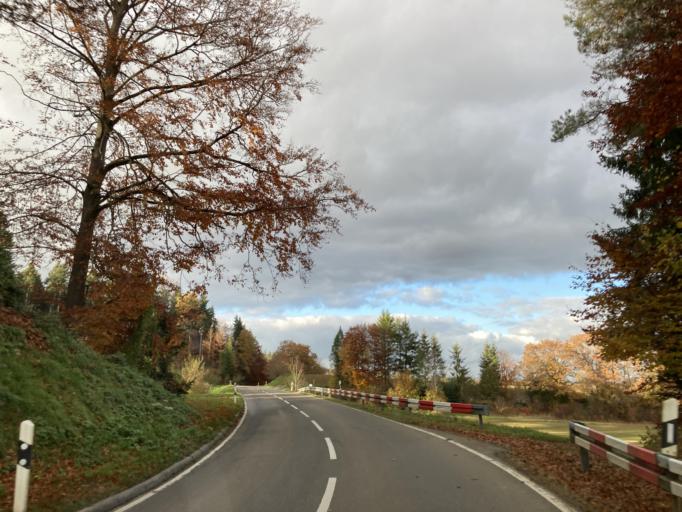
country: DE
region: Baden-Wuerttemberg
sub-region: Karlsruhe Region
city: Empfingen
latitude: 48.4095
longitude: 8.7502
